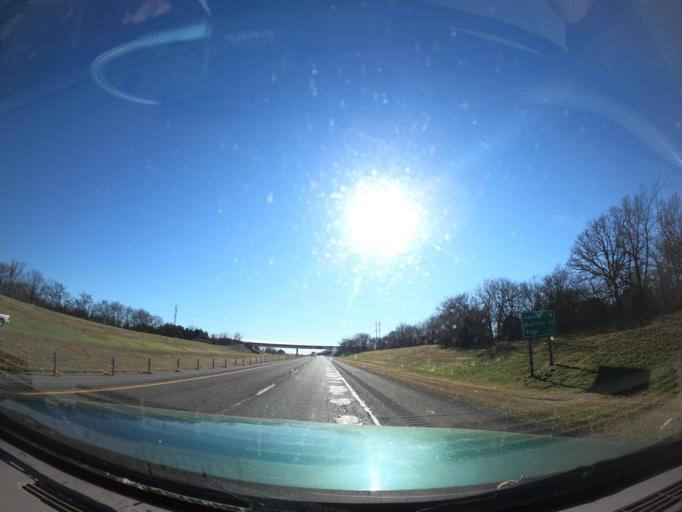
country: US
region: Oklahoma
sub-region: McIntosh County
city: Checotah
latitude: 35.3934
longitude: -95.5652
